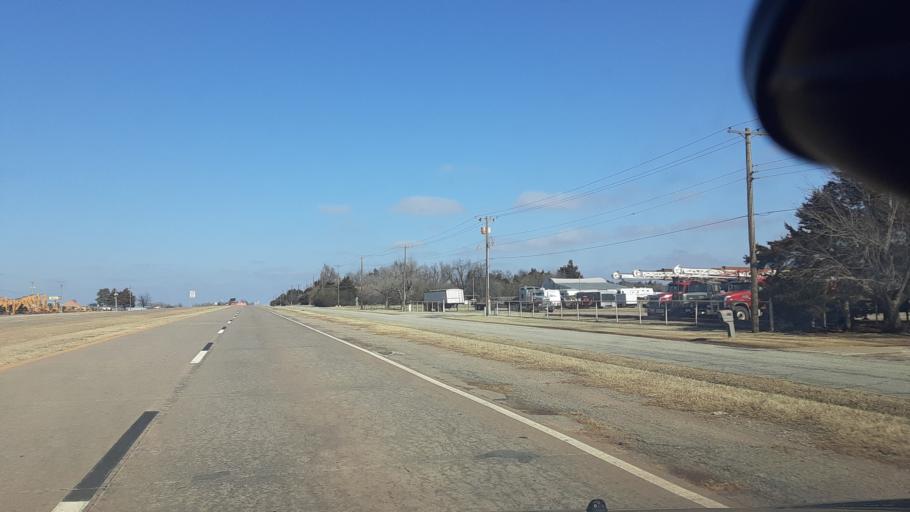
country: US
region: Oklahoma
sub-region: Garfield County
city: Enid
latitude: 36.4525
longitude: -97.8729
